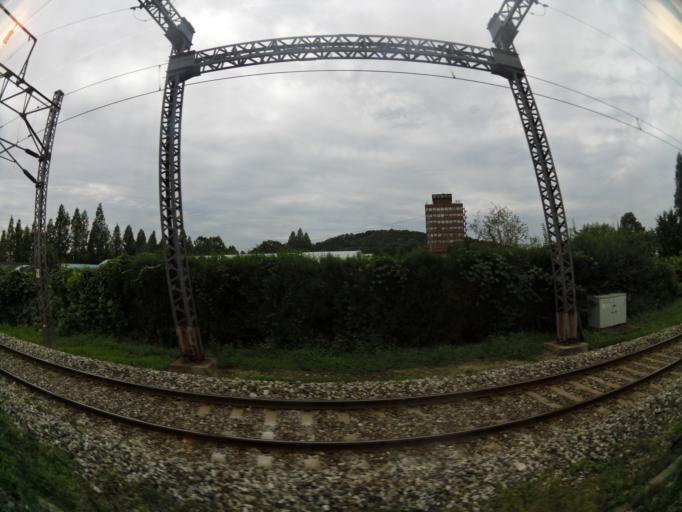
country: KR
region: Gyeonggi-do
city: Suwon-si
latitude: 37.2819
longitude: 126.9907
